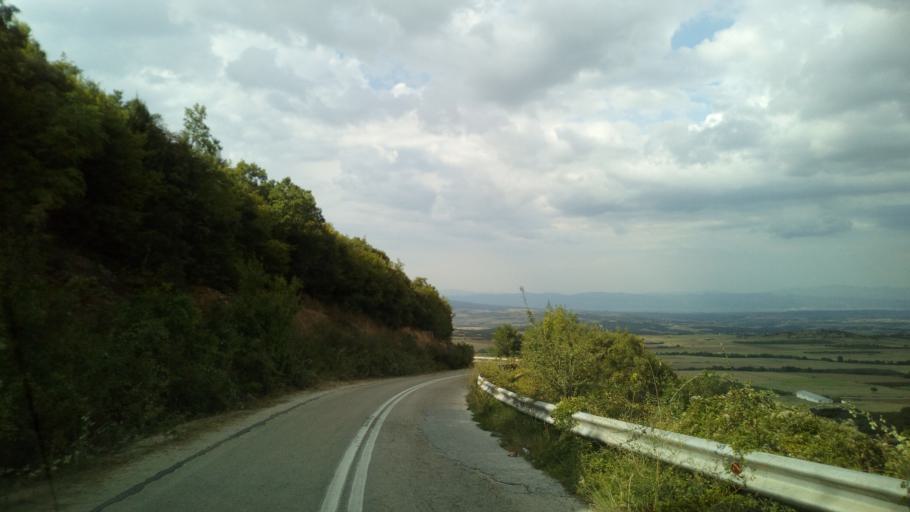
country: GR
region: Central Macedonia
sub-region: Nomos Chalkidikis
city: Galatista
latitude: 40.4942
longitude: 23.3905
